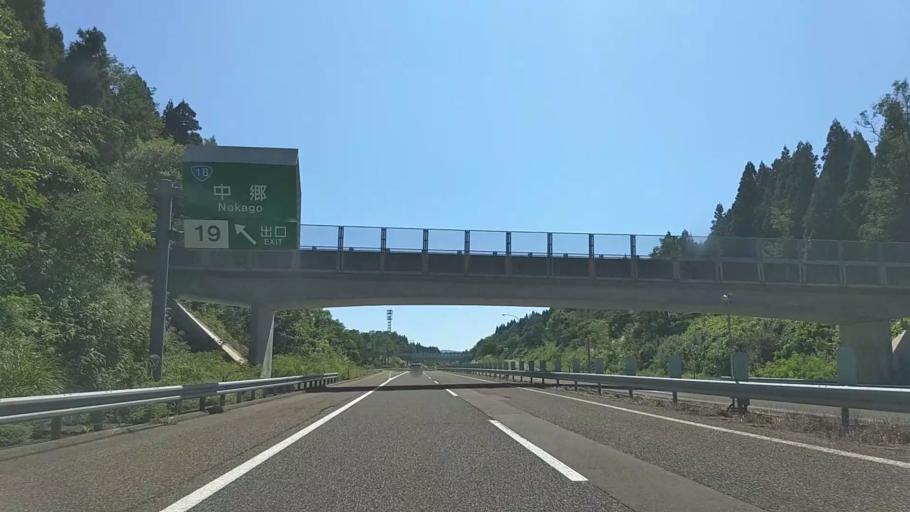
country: JP
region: Niigata
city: Arai
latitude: 36.9728
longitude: 138.2216
